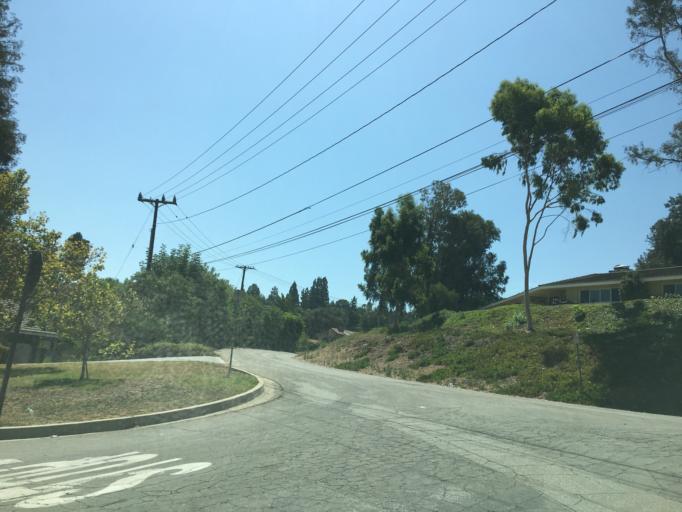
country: US
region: California
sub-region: Los Angeles County
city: Charter Oak
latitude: 34.0705
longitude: -117.8356
